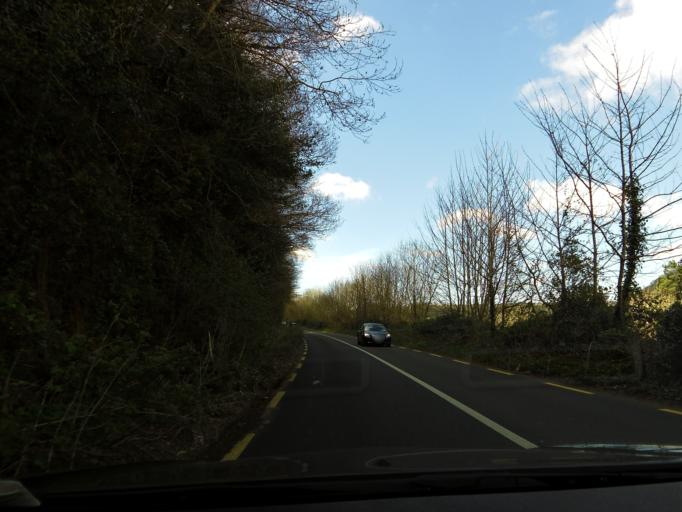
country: IE
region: Leinster
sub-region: Wicklow
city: Arklow
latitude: 52.8266
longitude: -6.2206
